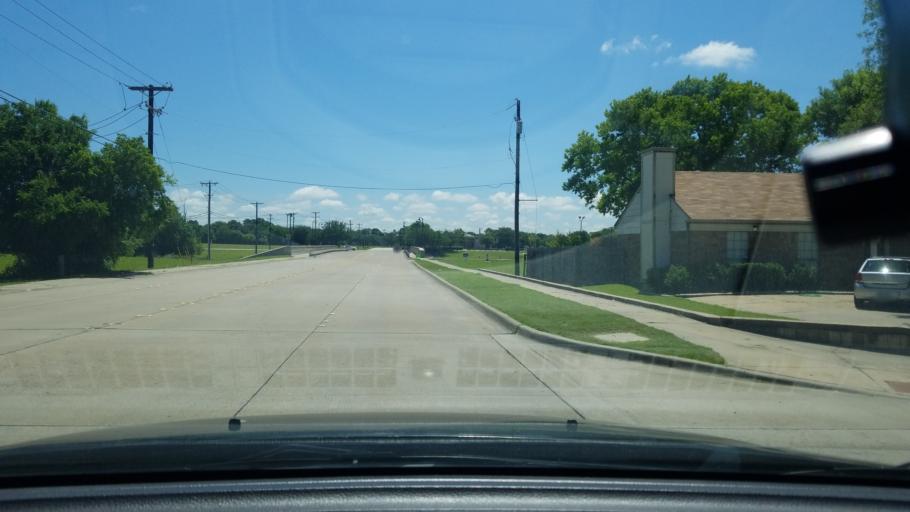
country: US
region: Texas
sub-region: Dallas County
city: Mesquite
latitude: 32.7976
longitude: -96.5984
